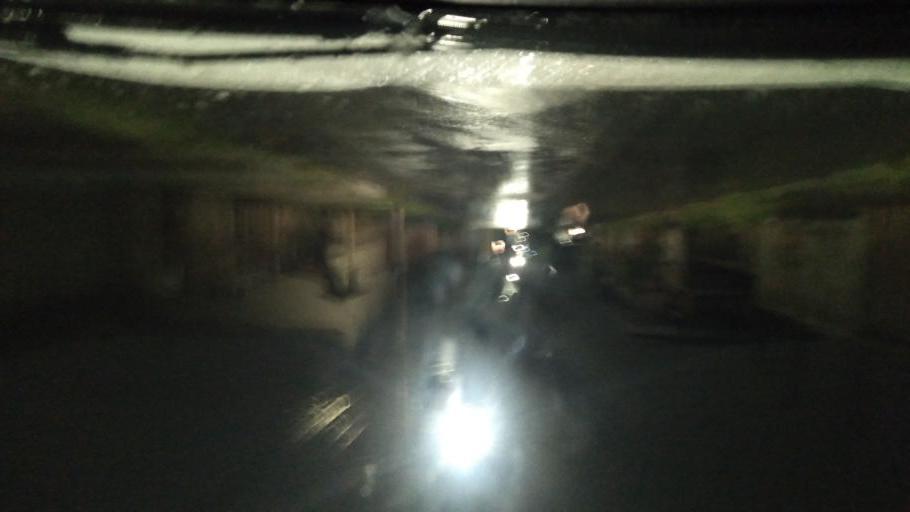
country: BR
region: Minas Gerais
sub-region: Belo Horizonte
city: Belo Horizonte
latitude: -19.8986
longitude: -43.9596
